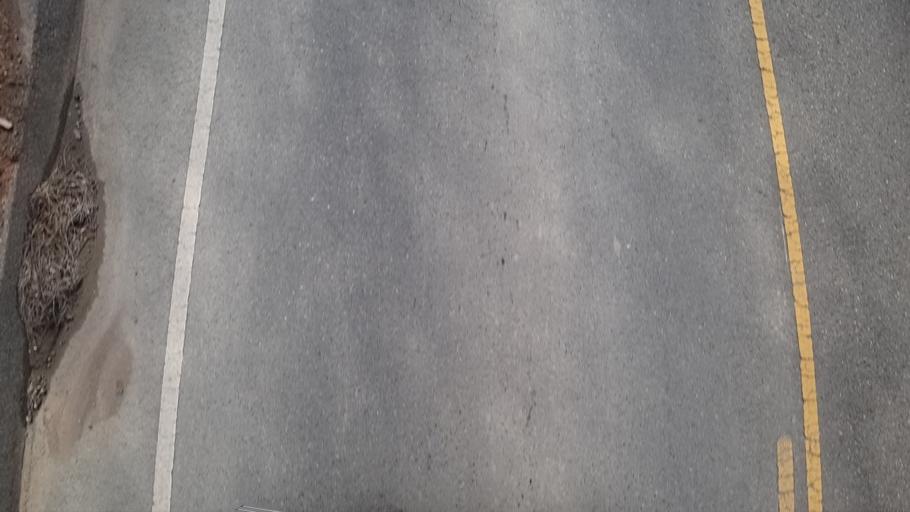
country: US
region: California
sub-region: Butte County
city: Oroville East
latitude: 39.4363
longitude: -121.4307
